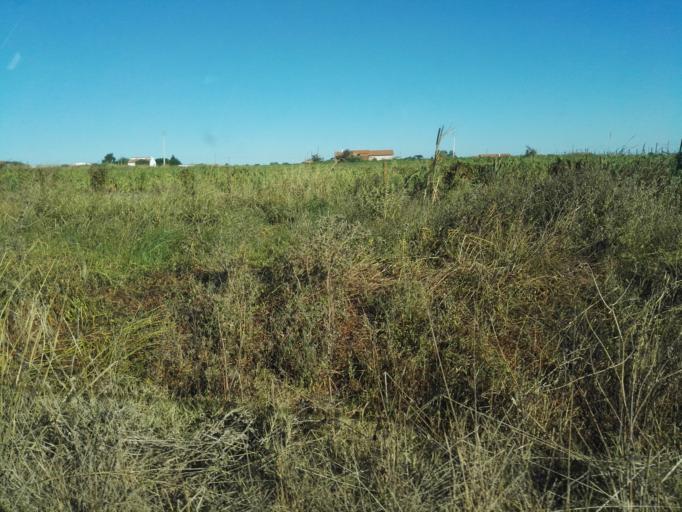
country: PT
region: Santarem
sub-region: Benavente
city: Benavente
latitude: 38.9382
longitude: -8.8088
